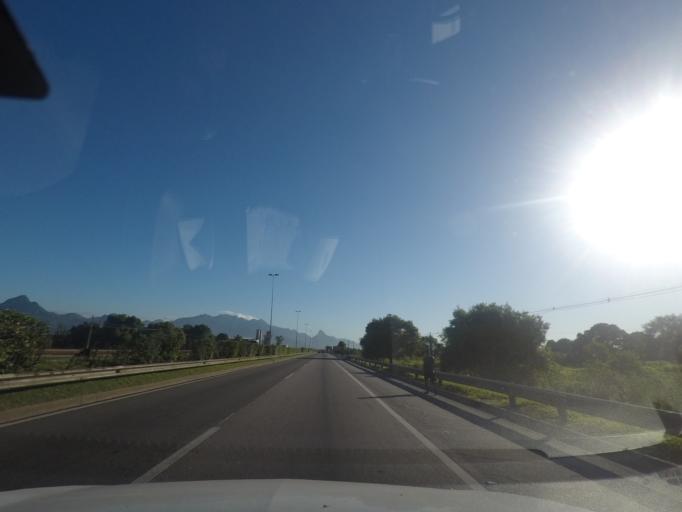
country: BR
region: Rio de Janeiro
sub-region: Duque De Caxias
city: Duque de Caxias
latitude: -22.6576
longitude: -43.2478
